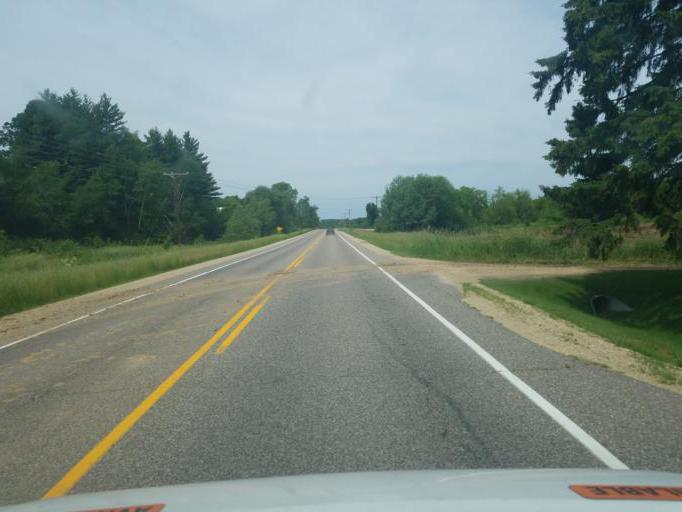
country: US
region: Wisconsin
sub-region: Juneau County
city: Elroy
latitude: 43.7656
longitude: -90.2413
